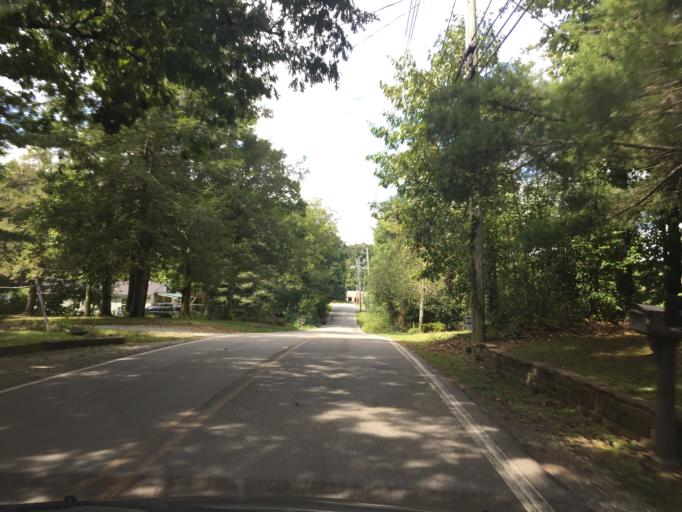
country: US
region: Tennessee
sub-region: Hamilton County
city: Signal Mountain
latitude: 35.1373
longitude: -85.3278
